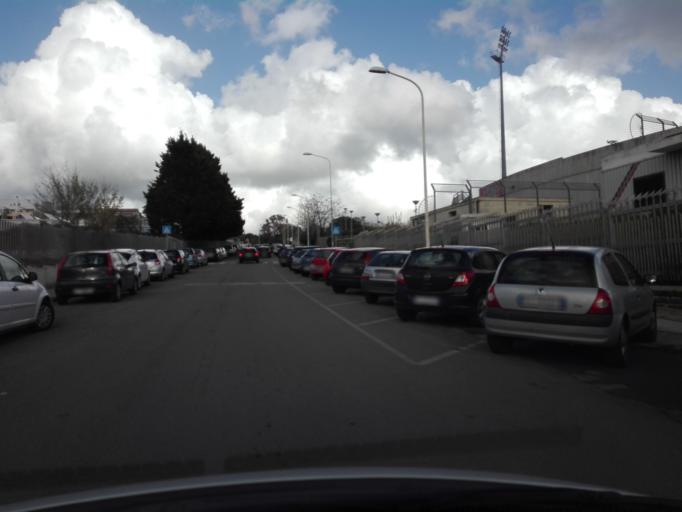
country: IT
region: Sardinia
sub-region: Provincia di Sassari
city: Sassari
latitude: 40.7191
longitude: 8.5795
